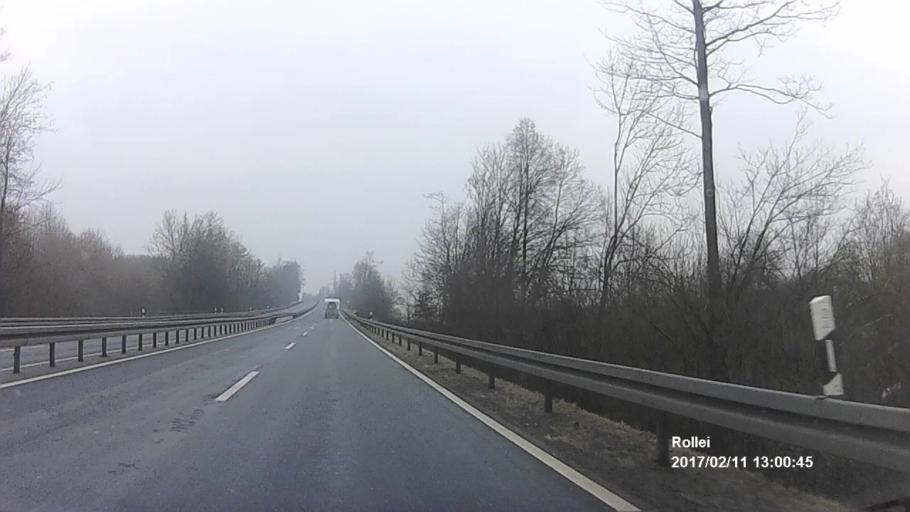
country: DE
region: Lower Saxony
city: Gittelde
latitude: 51.8162
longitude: 10.1889
